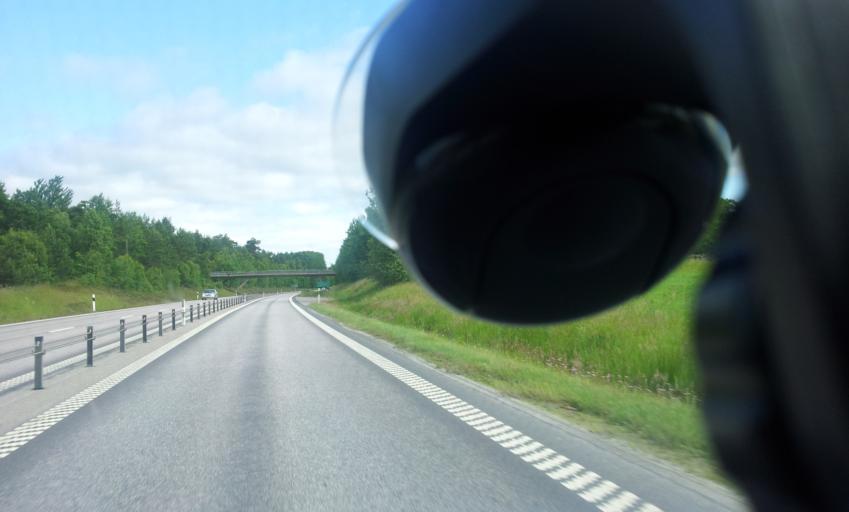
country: SE
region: Kalmar
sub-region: Kalmar Kommun
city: Lindsdal
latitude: 56.7471
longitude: 16.3052
